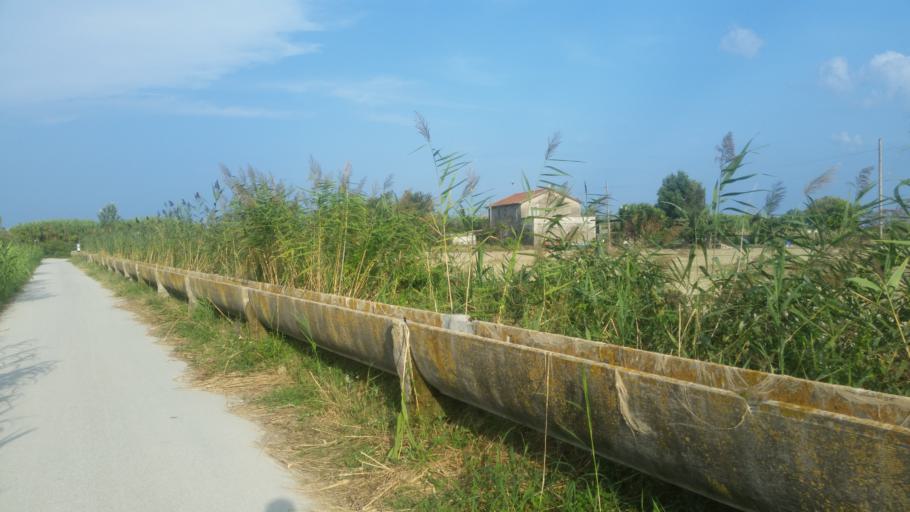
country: IT
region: The Marches
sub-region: Provincia di Ascoli Piceno
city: San Benedetto del Tronto
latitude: 42.9039
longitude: 13.9057
